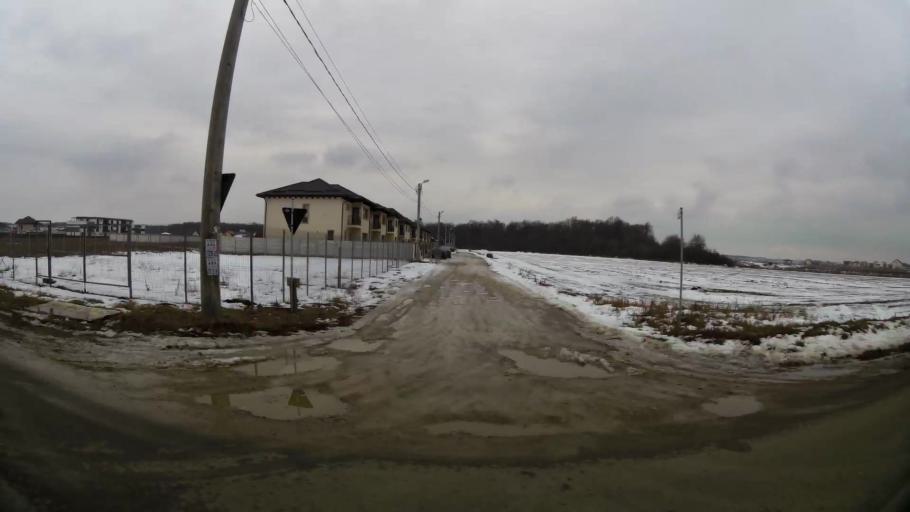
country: RO
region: Ilfov
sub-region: Comuna Tunari
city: Tunari
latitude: 44.5519
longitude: 26.1115
